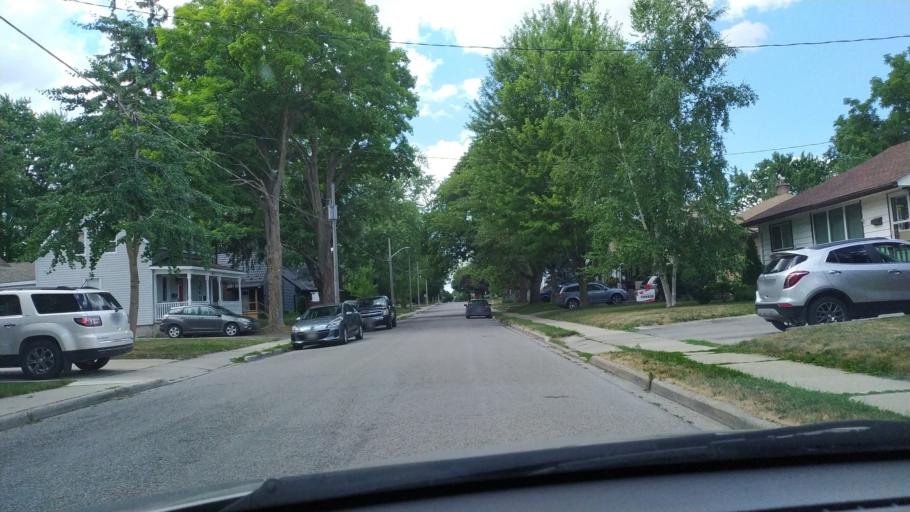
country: CA
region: Ontario
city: Stratford
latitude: 43.3752
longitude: -80.9952
